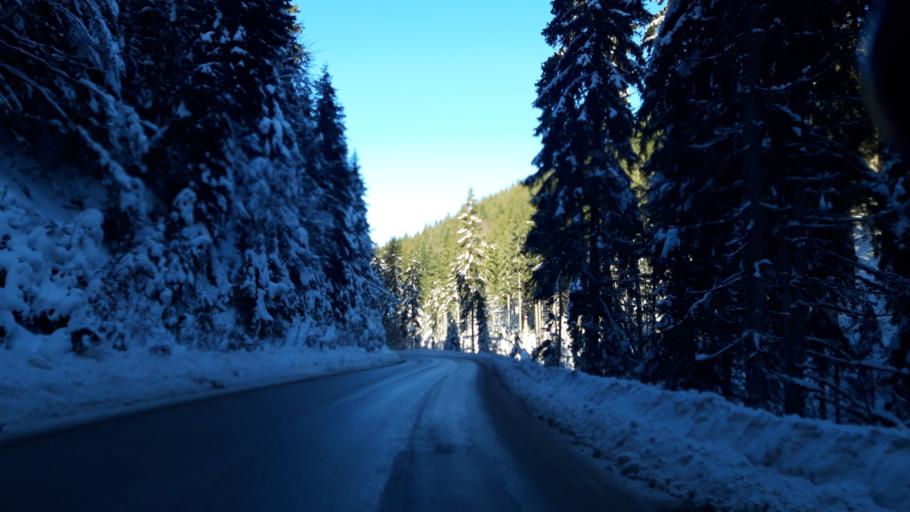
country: BA
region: Republika Srpska
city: Koran
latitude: 43.7476
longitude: 18.5566
